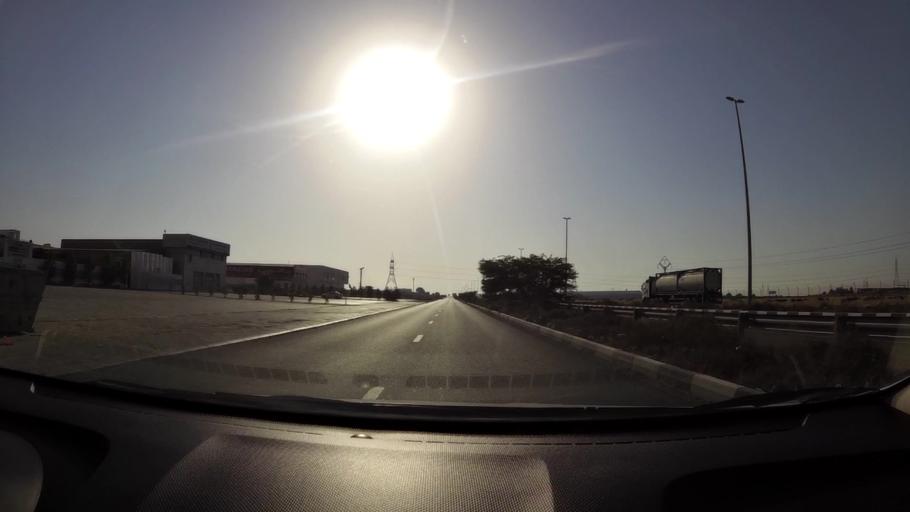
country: AE
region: Ajman
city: Ajman
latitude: 25.4435
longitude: 55.5441
